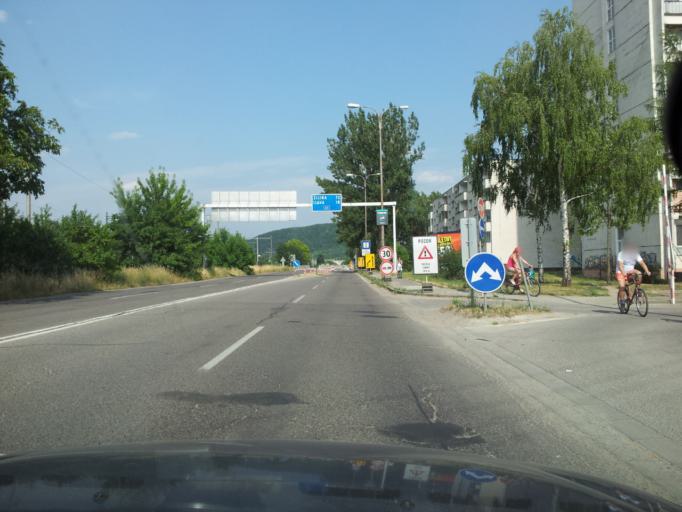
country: SK
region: Trenciansky
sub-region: Okres Trencin
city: Trencin
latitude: 48.8951
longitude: 18.0674
